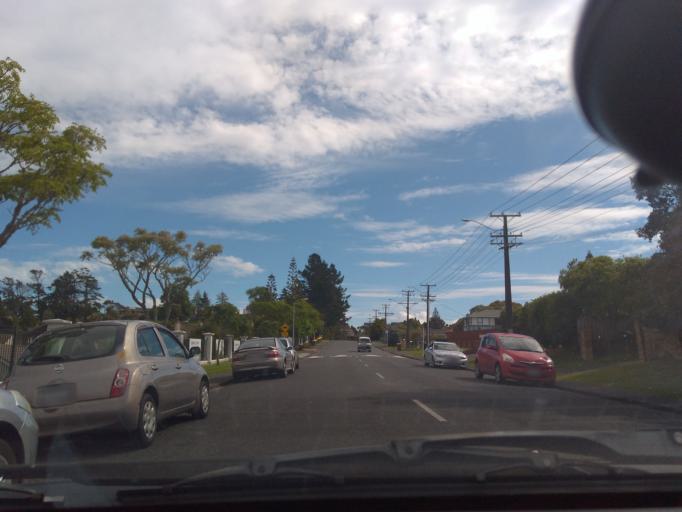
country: NZ
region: Auckland
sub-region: Auckland
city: Titirangi
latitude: -36.9350
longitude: 174.6720
